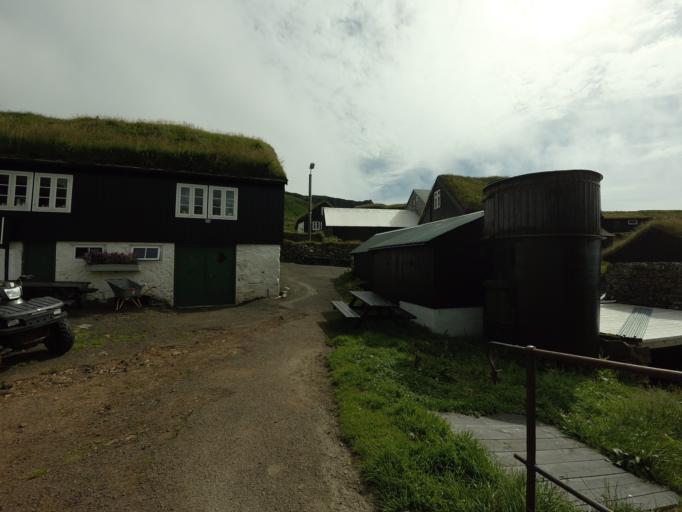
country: FO
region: Vagar
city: Sorvagur
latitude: 62.1032
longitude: -7.6448
